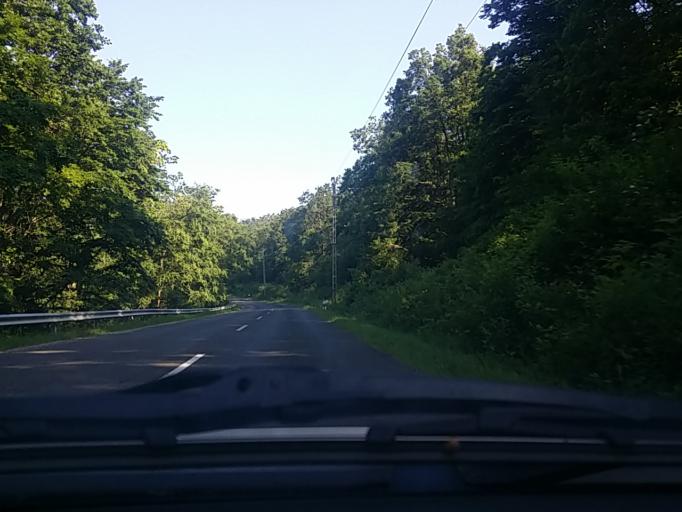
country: HU
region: Pest
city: Pilisszentkereszt
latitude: 47.7087
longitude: 18.8821
